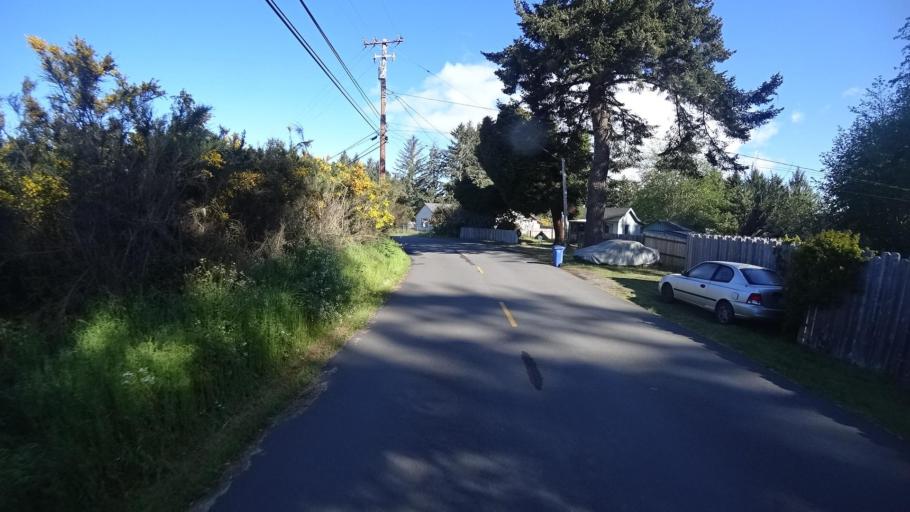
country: US
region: California
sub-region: Humboldt County
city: Westhaven-Moonstone
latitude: 41.0047
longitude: -124.1011
